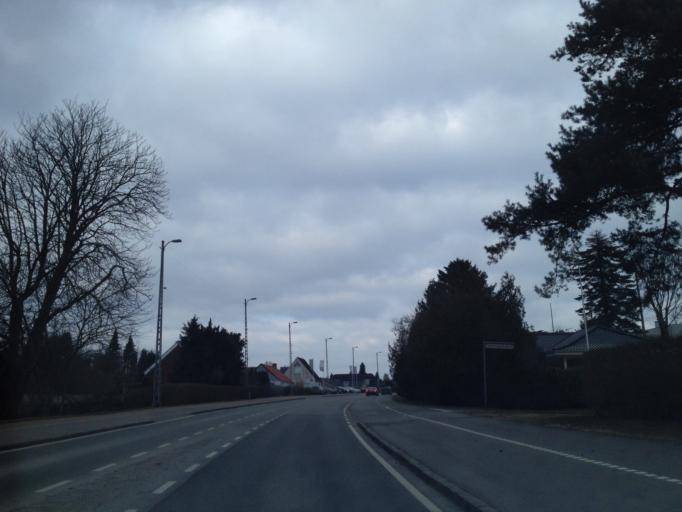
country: DK
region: Capital Region
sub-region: Fredensborg Kommune
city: Humlebaek
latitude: 55.9795
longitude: 12.5449
